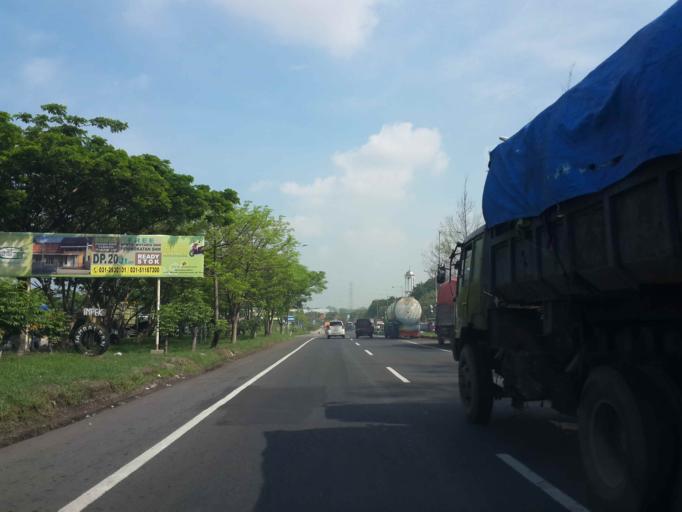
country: ID
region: East Java
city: Kebomas
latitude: -7.2000
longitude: 112.6458
